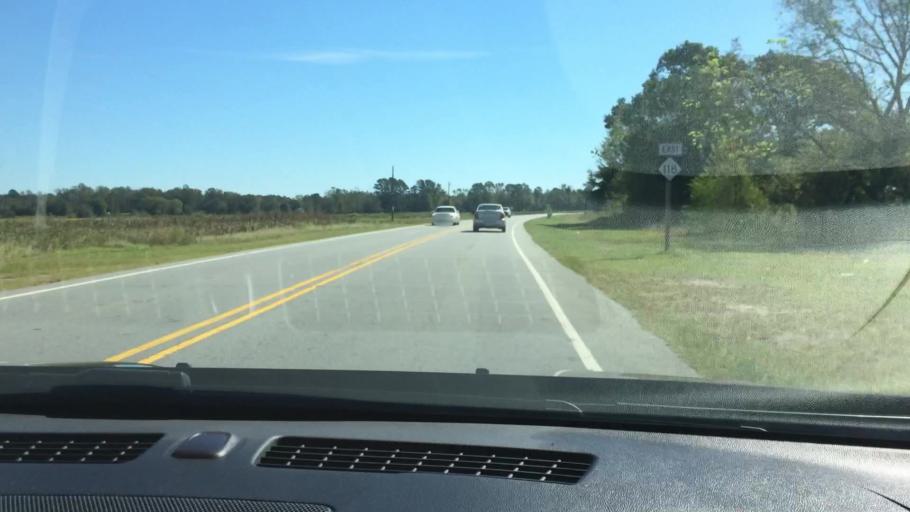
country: US
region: North Carolina
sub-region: Pitt County
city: Grifton
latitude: 35.3504
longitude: -77.3283
